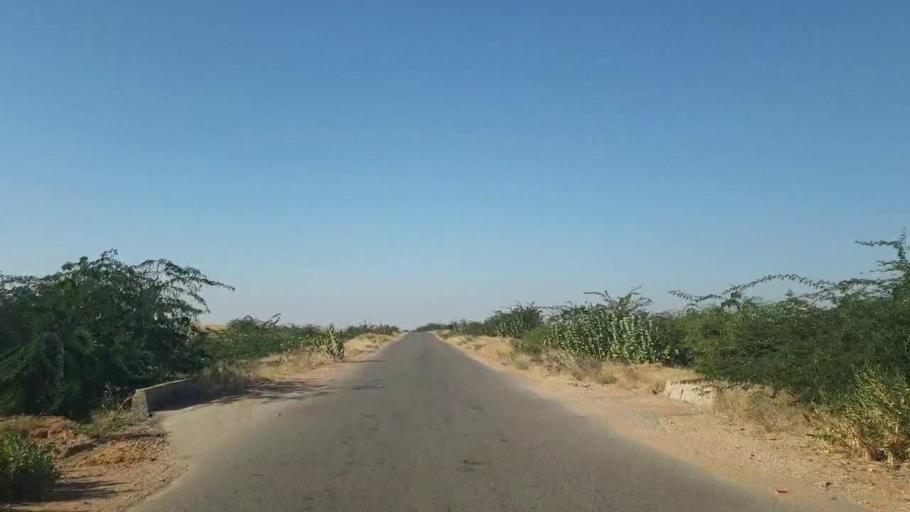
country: PK
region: Sindh
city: Malir Cantonment
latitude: 25.2688
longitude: 67.5942
